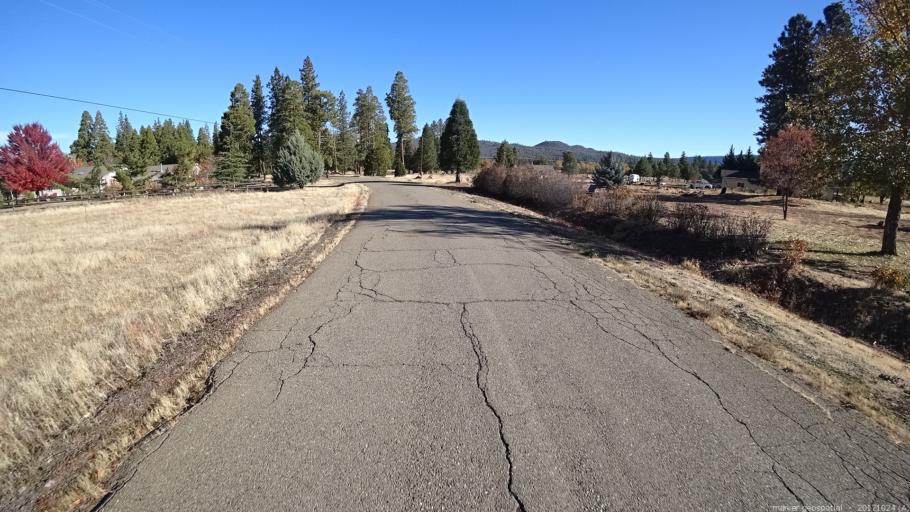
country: US
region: California
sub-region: Shasta County
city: Burney
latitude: 40.8361
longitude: -121.5141
